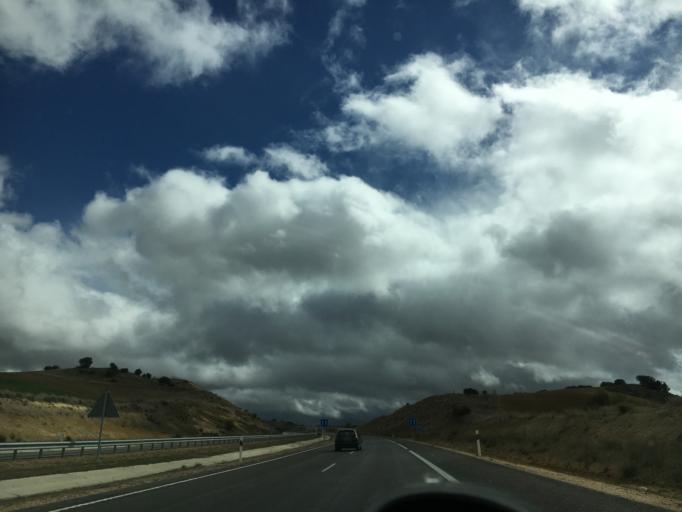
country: ES
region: Castille and Leon
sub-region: Provincia de Zamora
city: Corrales
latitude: 41.3289
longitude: -5.7271
